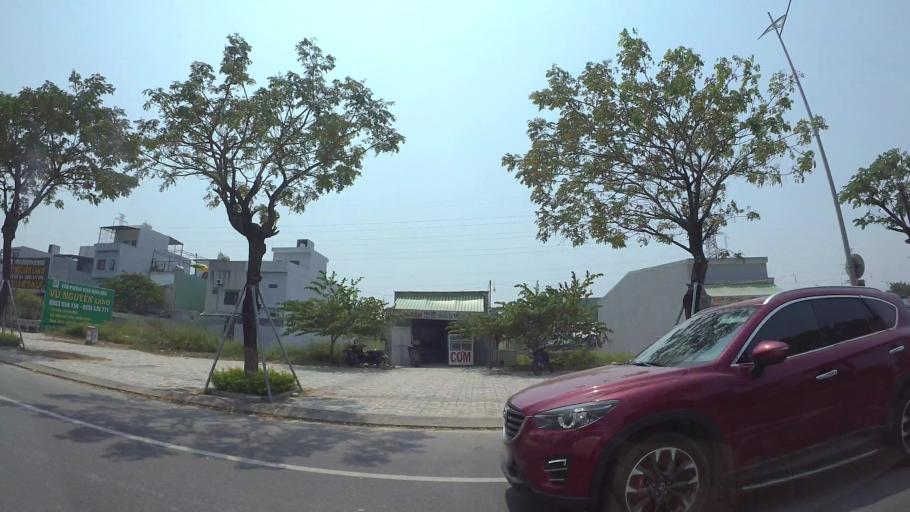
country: VN
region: Da Nang
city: Ngu Hanh Son
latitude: 16.0181
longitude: 108.2309
